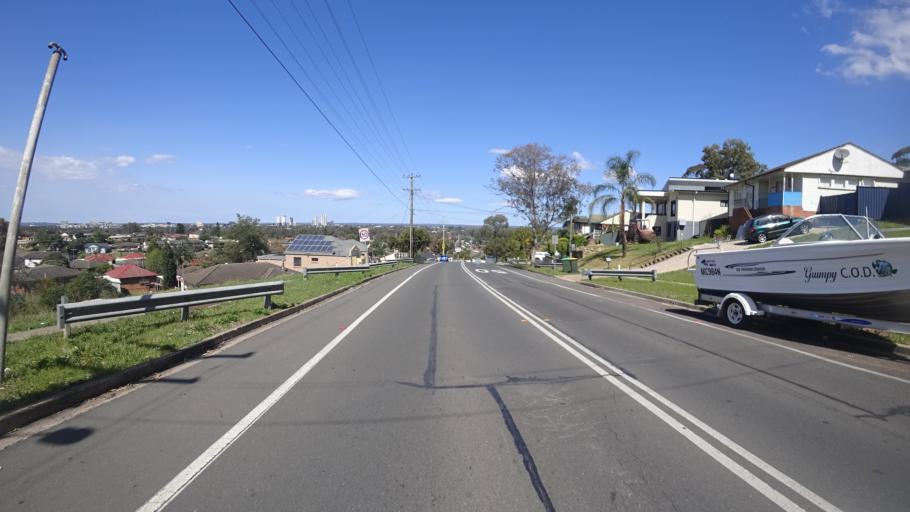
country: AU
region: New South Wales
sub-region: Liverpool
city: Miller
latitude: -33.9106
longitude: 150.8940
